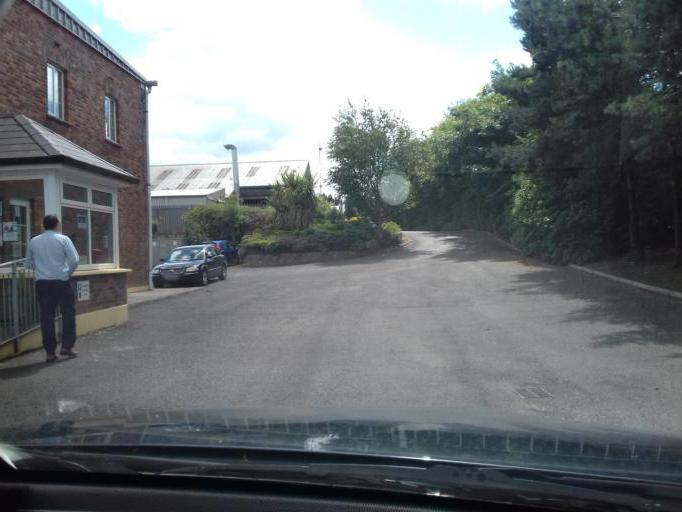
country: IE
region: Munster
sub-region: Waterford
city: Tra Mhor
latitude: 52.1771
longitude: -7.2514
